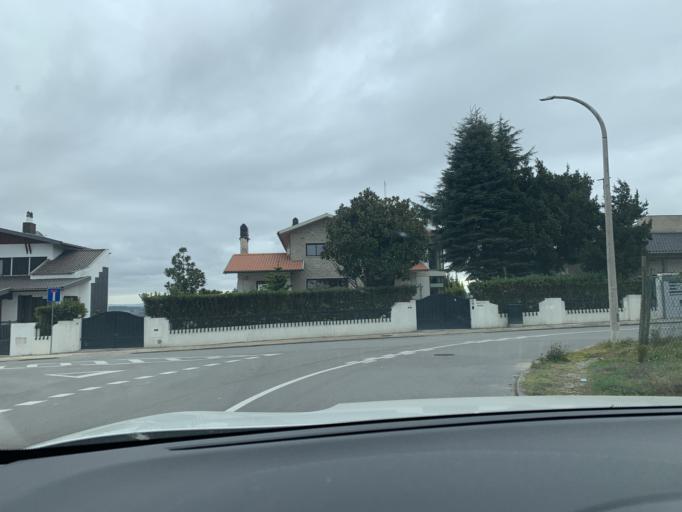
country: PT
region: Viseu
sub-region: Viseu
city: Rio de Loba
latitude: 40.6394
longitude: -7.8571
